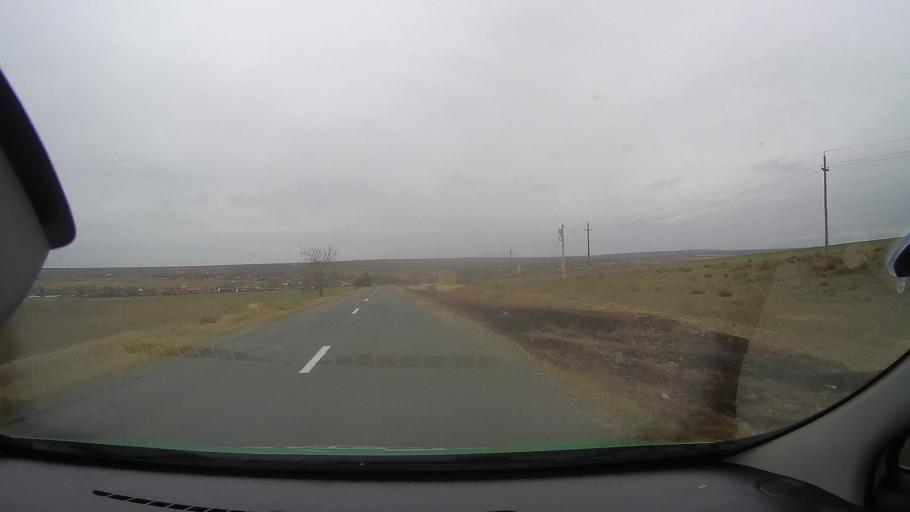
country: RO
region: Constanta
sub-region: Comuna Targusor
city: Targusor
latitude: 44.4870
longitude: 28.3658
